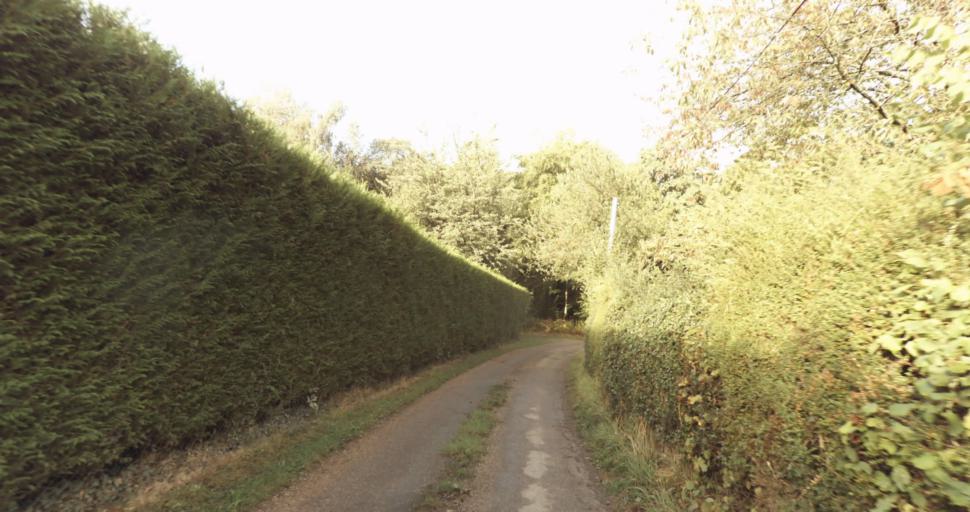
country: FR
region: Lower Normandy
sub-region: Departement de l'Orne
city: Vimoutiers
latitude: 48.8942
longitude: 0.2488
